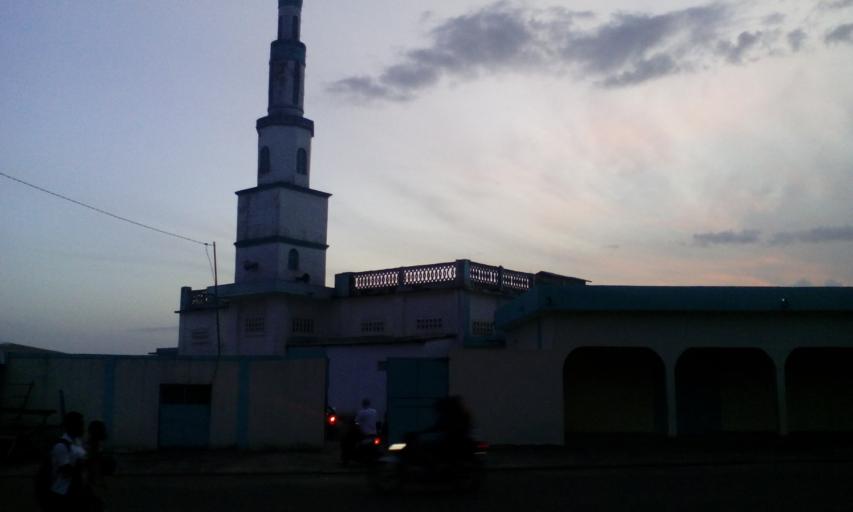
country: CI
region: Zanzan
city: Bondoukou
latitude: 8.0415
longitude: -2.7990
